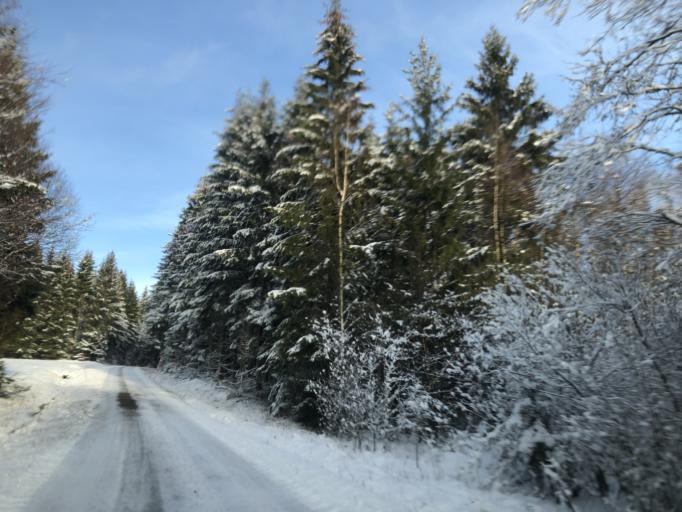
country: SE
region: Vaestra Goetaland
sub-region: Ulricehamns Kommun
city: Ulricehamn
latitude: 57.7403
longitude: 13.4962
